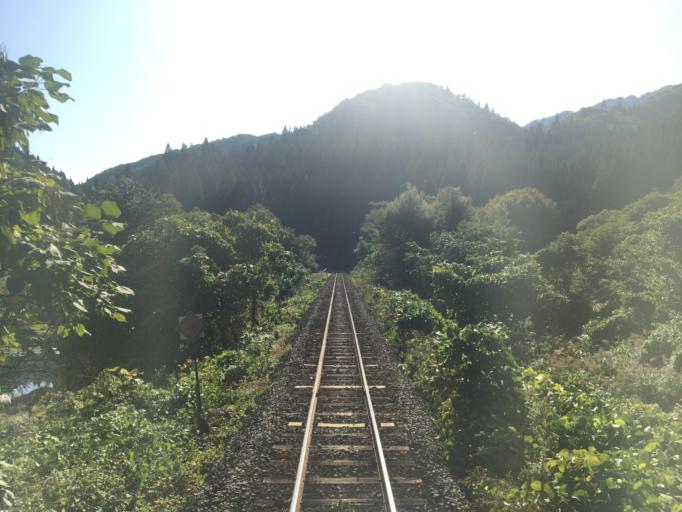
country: JP
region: Akita
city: Kakunodatemachi
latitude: 39.7241
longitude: 140.5569
